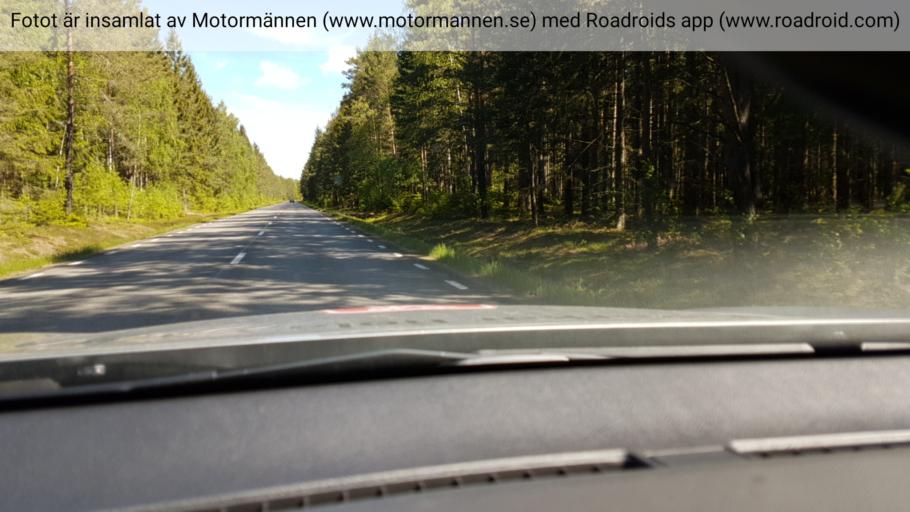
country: SE
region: Vaestra Goetaland
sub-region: Karlsborgs Kommun
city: Molltorp
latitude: 58.3998
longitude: 14.3589
